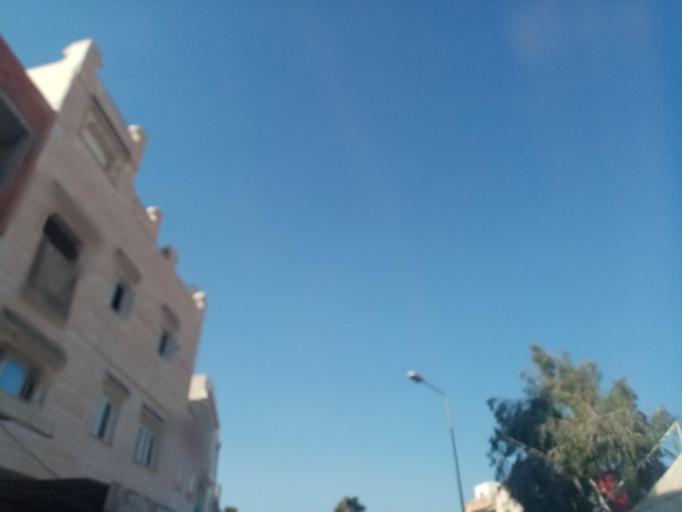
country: TN
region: Qabis
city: Gabes
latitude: 33.8900
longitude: 10.0940
